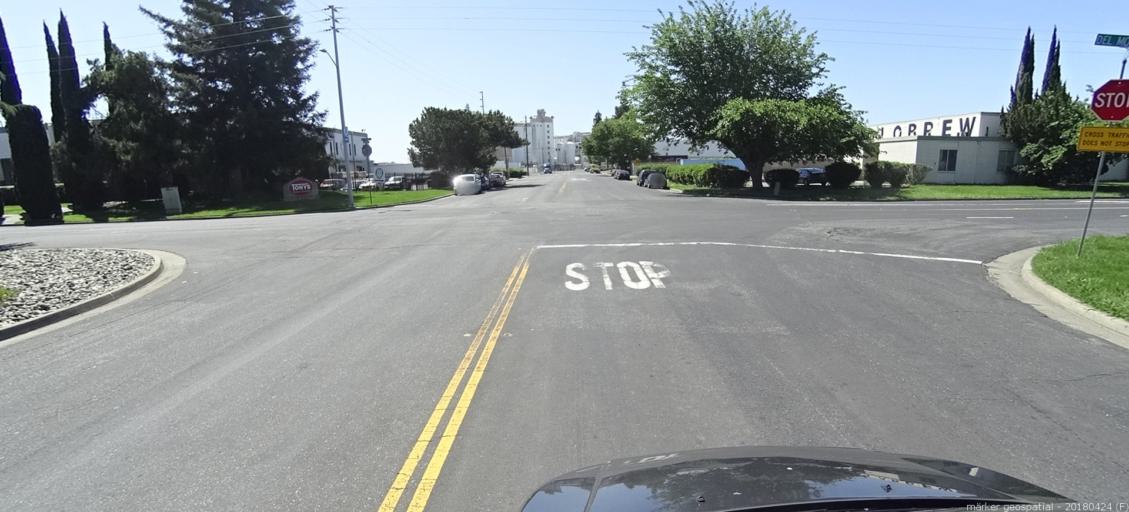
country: US
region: California
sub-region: Yolo County
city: West Sacramento
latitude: 38.5701
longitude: -121.5414
